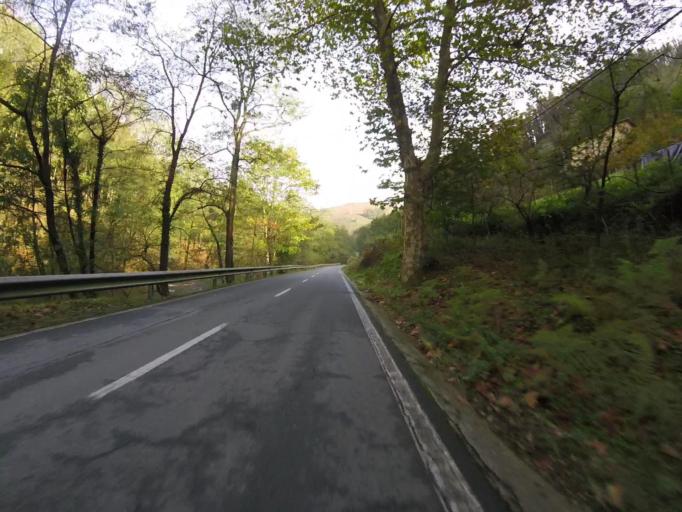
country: ES
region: Navarre
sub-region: Provincia de Navarra
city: Goizueta
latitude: 43.1845
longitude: -1.8591
